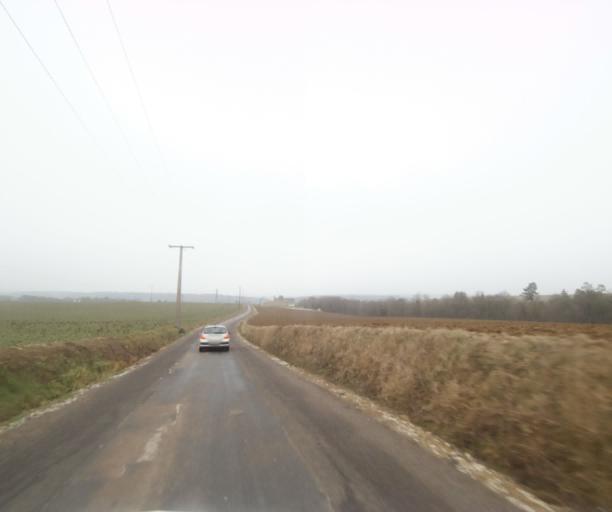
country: FR
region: Champagne-Ardenne
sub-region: Departement de la Haute-Marne
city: Bienville
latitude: 48.5405
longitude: 5.0647
